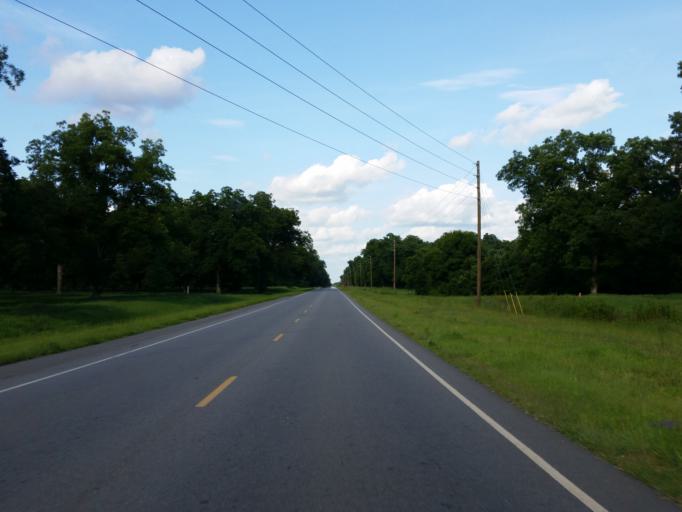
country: US
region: Georgia
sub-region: Crisp County
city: Cordele
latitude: 31.9596
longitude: -83.9657
